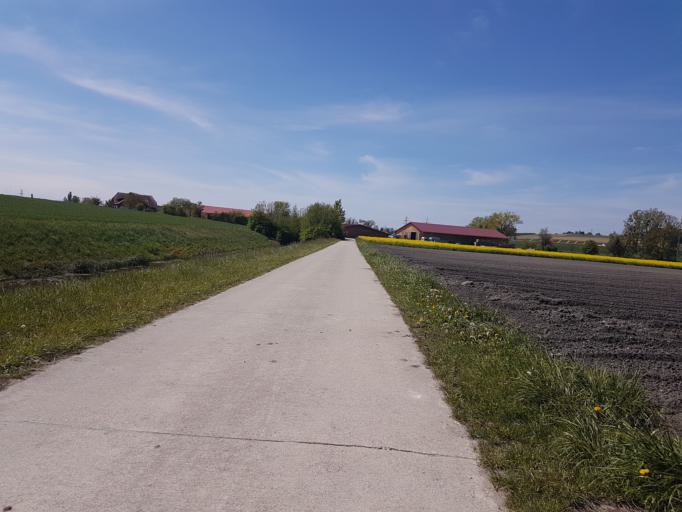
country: CH
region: Neuchatel
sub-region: Neuchatel District
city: Cornaux
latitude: 47.0297
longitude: 7.0371
